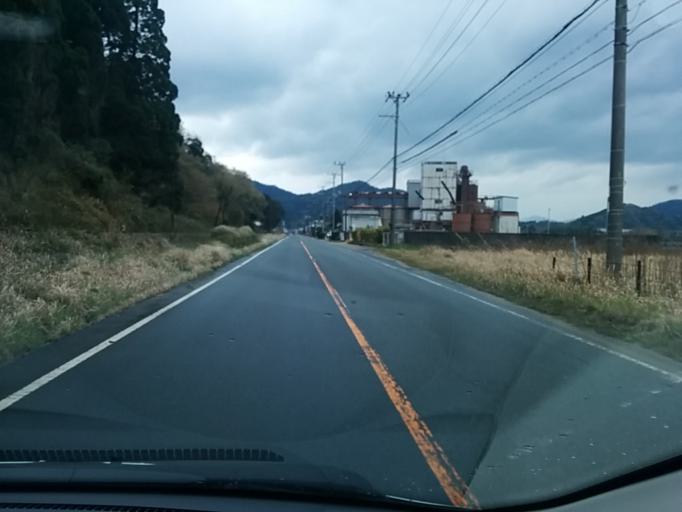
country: JP
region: Kyoto
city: Miyazu
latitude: 35.5608
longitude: 135.1682
